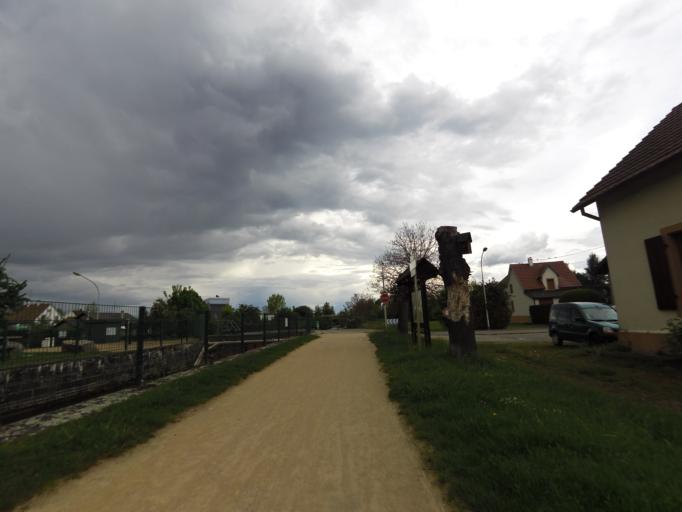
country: FR
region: Alsace
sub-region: Departement du Haut-Rhin
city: Rosenau
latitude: 47.6367
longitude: 7.5299
